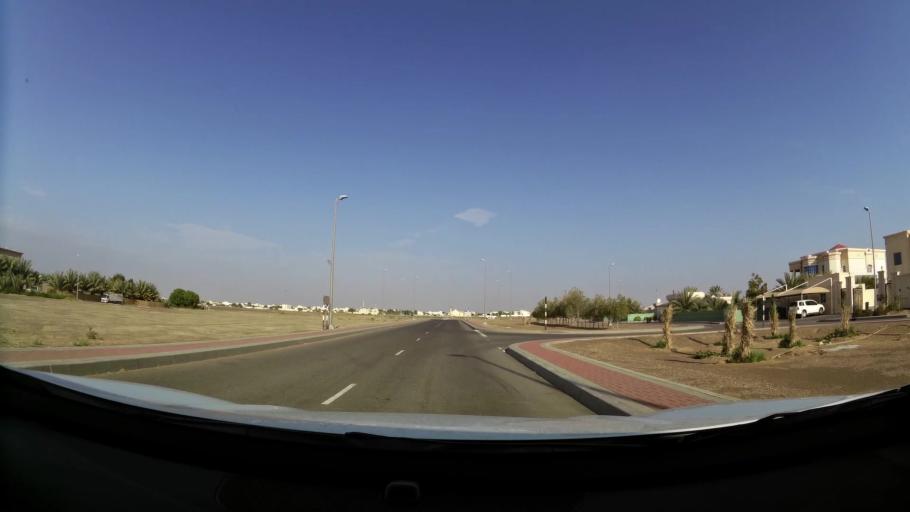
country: AE
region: Abu Dhabi
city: Al Ain
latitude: 24.0734
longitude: 55.8542
